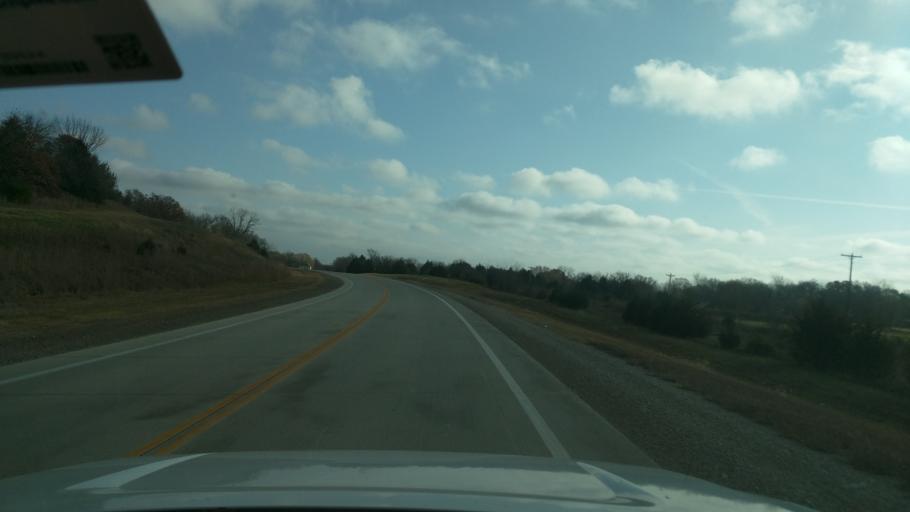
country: US
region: Kansas
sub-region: Montgomery County
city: Caney
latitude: 37.0674
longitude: -96.0213
